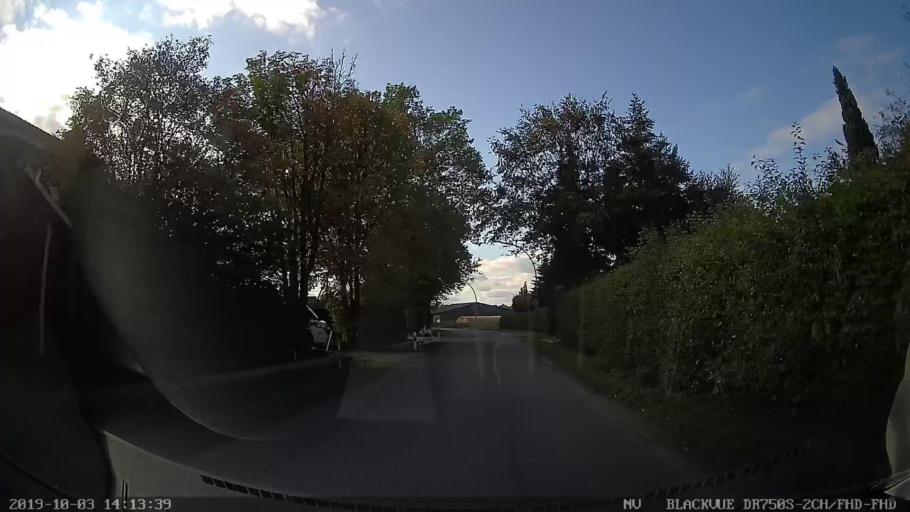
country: DE
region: Schleswig-Holstein
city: Rellingen
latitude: 53.6664
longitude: 9.8284
